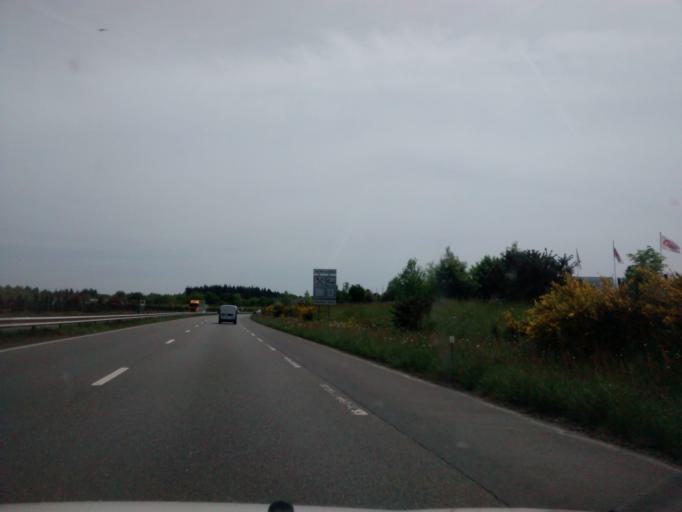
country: FR
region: Brittany
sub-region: Departement d'Ille-et-Vilaine
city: La Meziere
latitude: 48.2174
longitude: -1.7421
